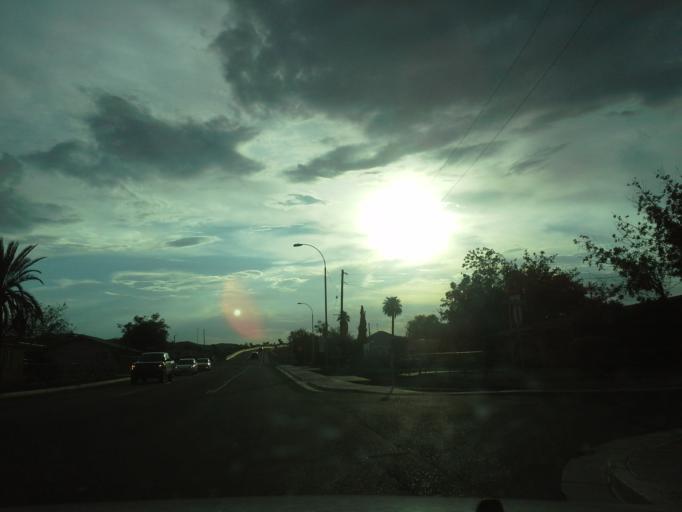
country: US
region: Arizona
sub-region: Maricopa County
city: Guadalupe
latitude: 33.3638
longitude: -111.9640
